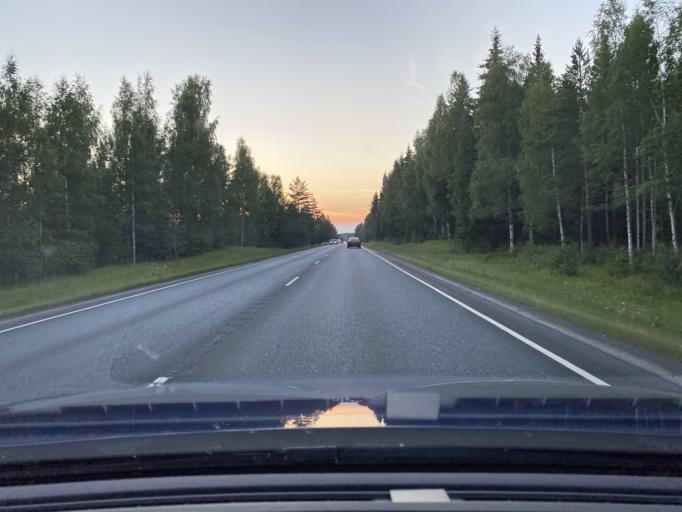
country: FI
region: Pirkanmaa
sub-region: Luoteis-Pirkanmaa
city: Ikaalinen
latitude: 61.7997
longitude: 22.9746
